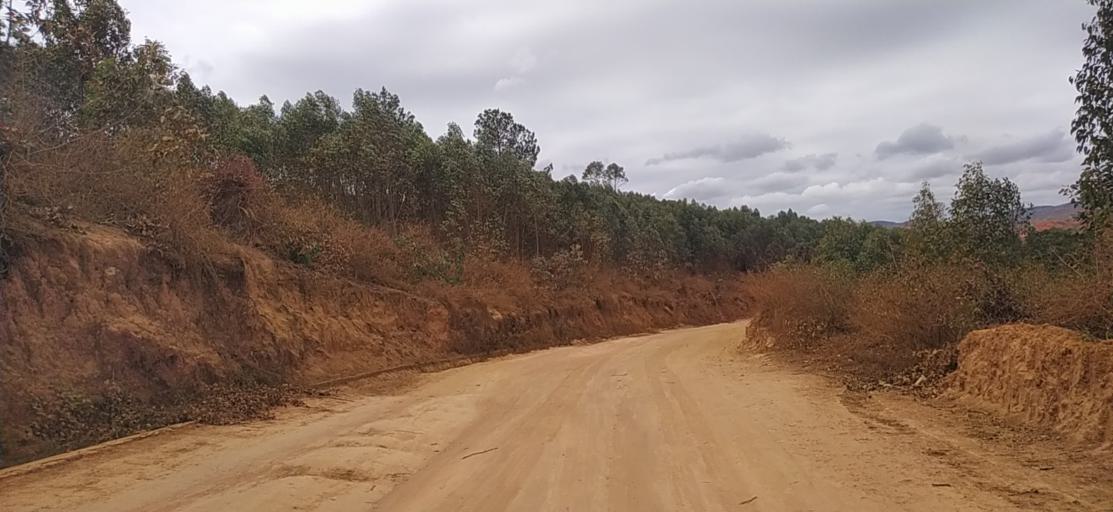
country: MG
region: Alaotra Mangoro
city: Ambatondrazaka
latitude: -18.0063
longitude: 48.2594
